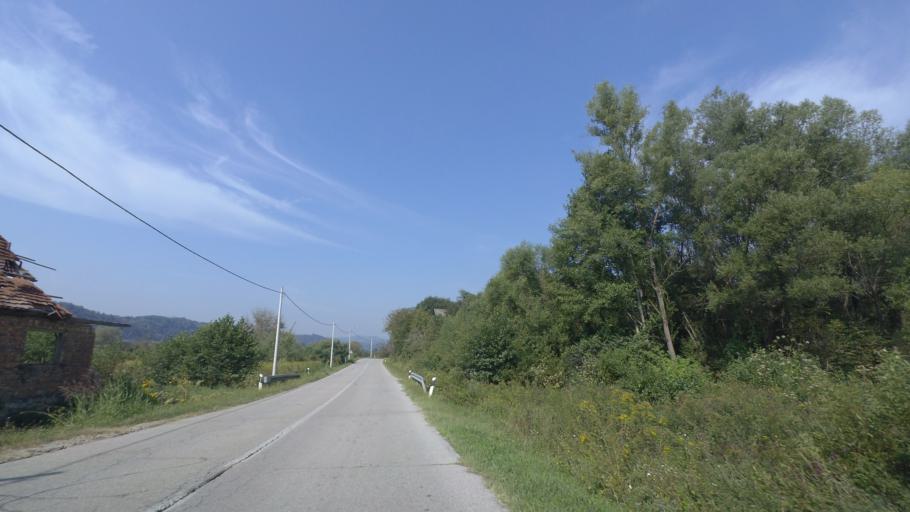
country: BA
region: Republika Srpska
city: Knezica
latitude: 45.2112
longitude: 16.6637
